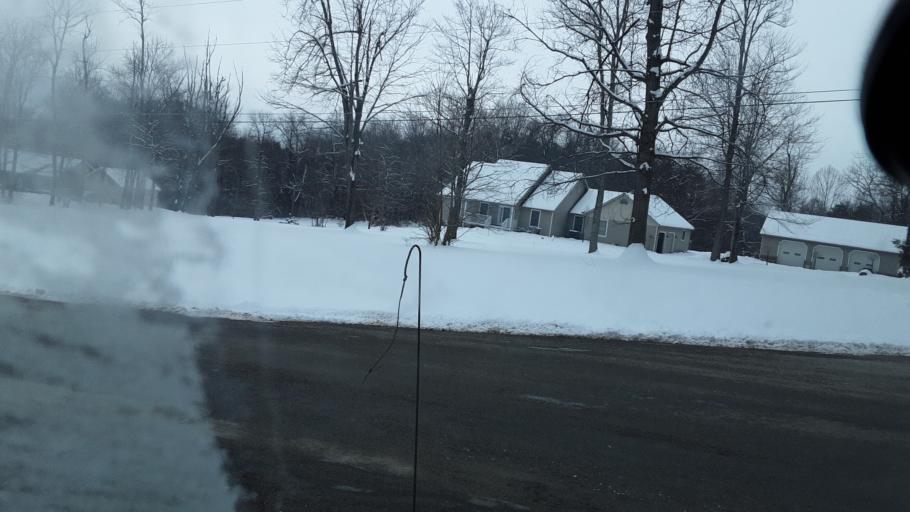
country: US
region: Ohio
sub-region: Perry County
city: Thornport
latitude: 39.9603
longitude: -82.3414
